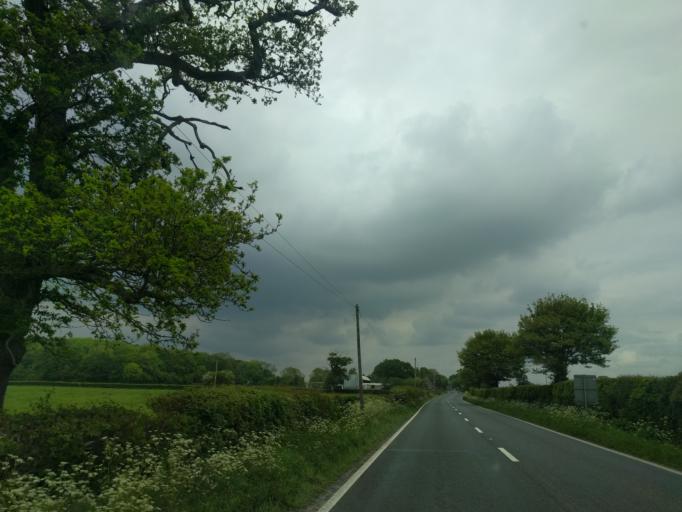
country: GB
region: England
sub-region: Somerset
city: Castle Cary
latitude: 51.0972
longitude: -2.5994
